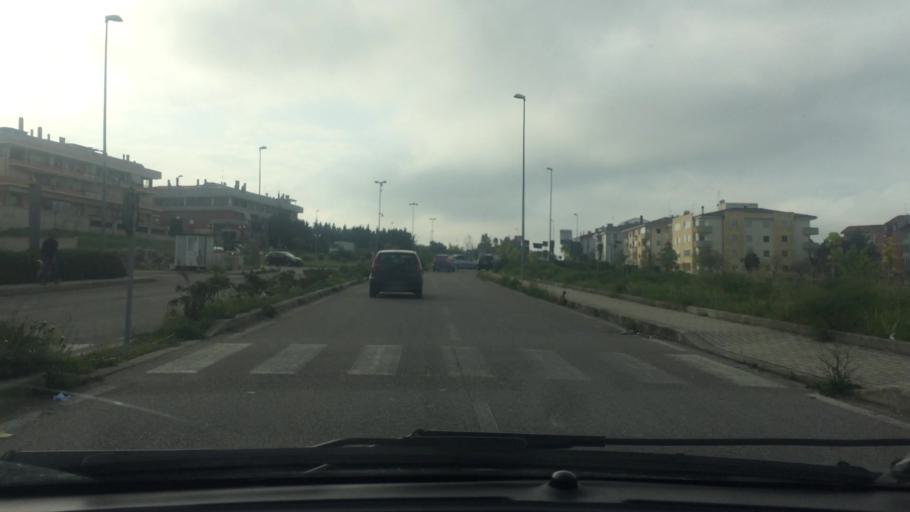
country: IT
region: Basilicate
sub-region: Provincia di Matera
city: Matera
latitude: 40.6846
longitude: 16.5750
